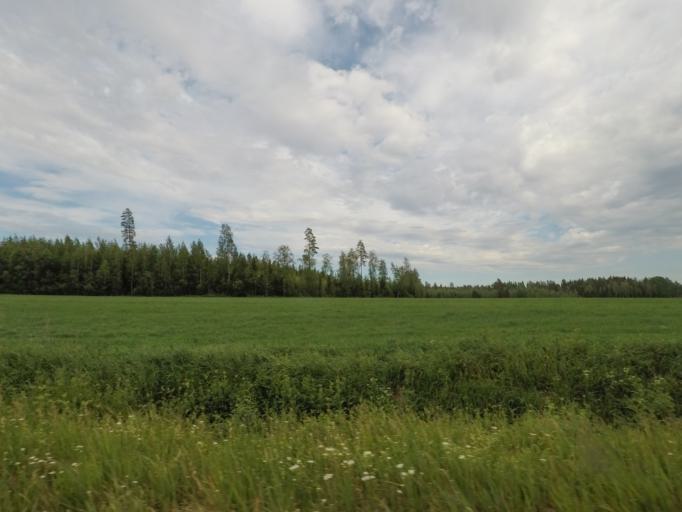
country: FI
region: Paijanne Tavastia
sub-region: Lahti
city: Hollola
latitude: 60.8258
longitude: 25.4883
